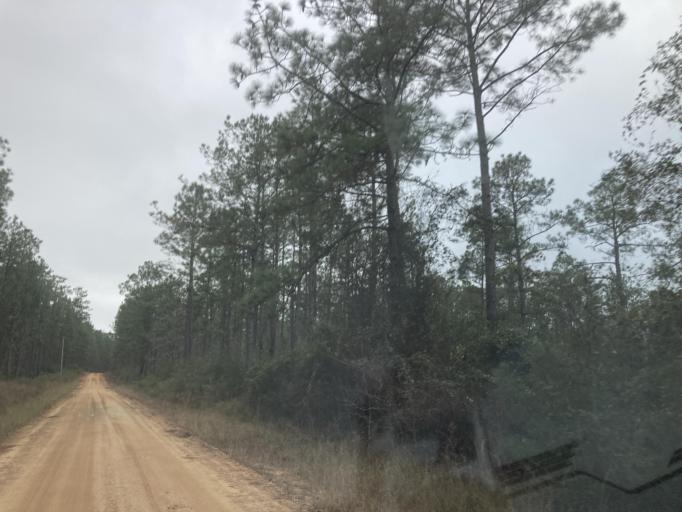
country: US
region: Mississippi
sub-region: Jackson County
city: Latimer
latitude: 30.6872
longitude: -88.9078
